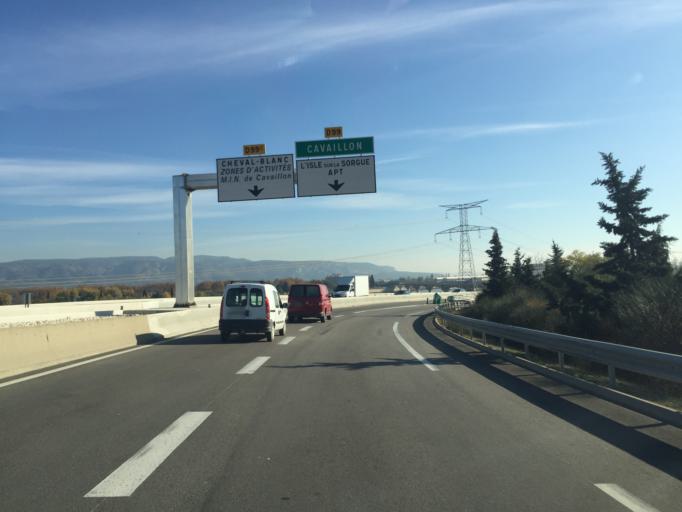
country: FR
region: Provence-Alpes-Cote d'Azur
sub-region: Departement du Vaucluse
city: Cavaillon
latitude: 43.8229
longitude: 5.0301
